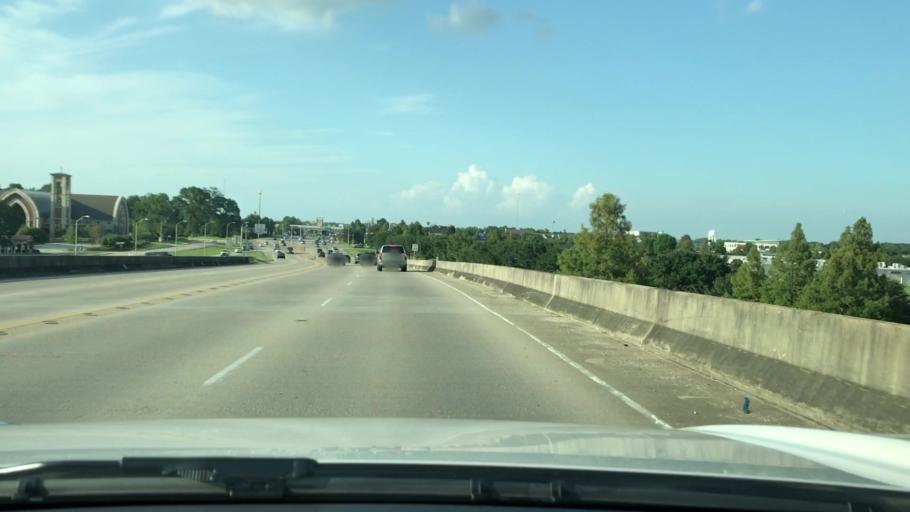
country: US
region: Louisiana
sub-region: East Baton Rouge Parish
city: Village Saint George
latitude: 30.3760
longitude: -91.0689
